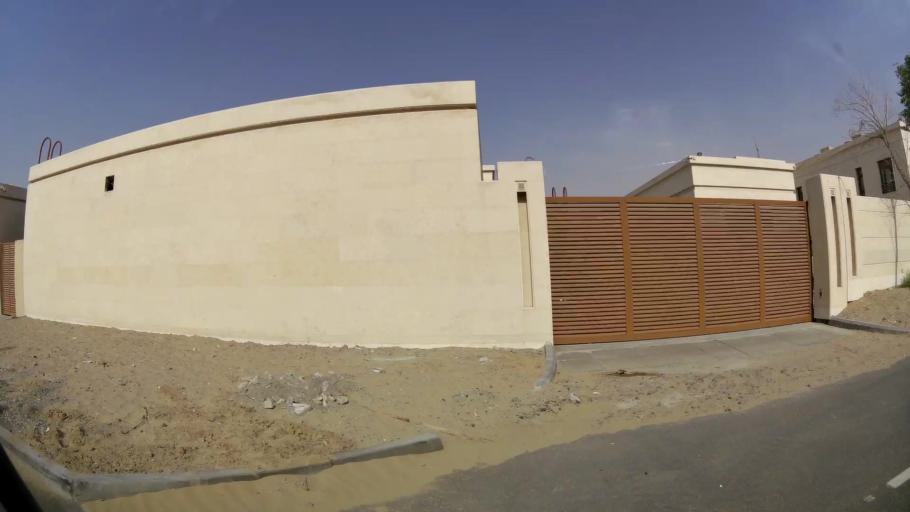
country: AE
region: Ash Shariqah
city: Sharjah
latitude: 25.2603
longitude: 55.4623
